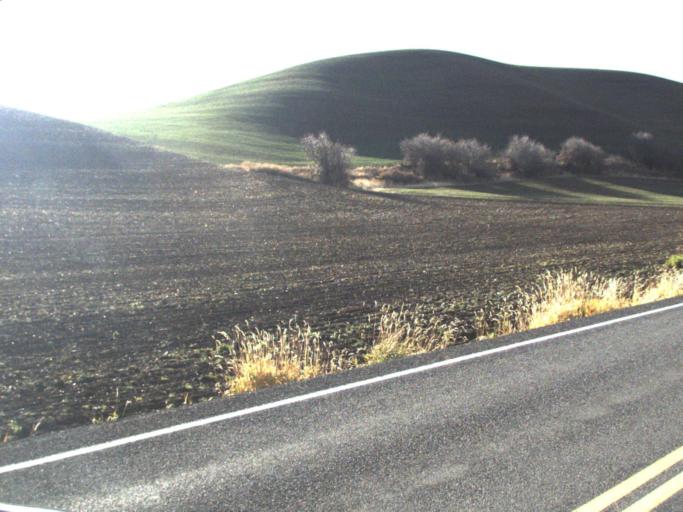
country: US
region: Washington
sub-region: Whitman County
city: Colfax
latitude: 46.7484
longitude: -117.4600
